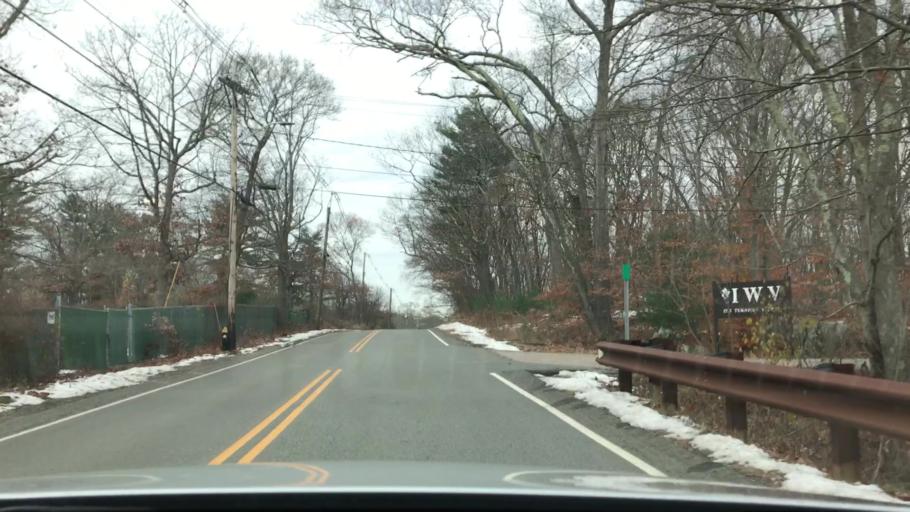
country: US
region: Massachusetts
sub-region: Norfolk County
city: Randolph
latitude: 42.1569
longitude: -71.0731
